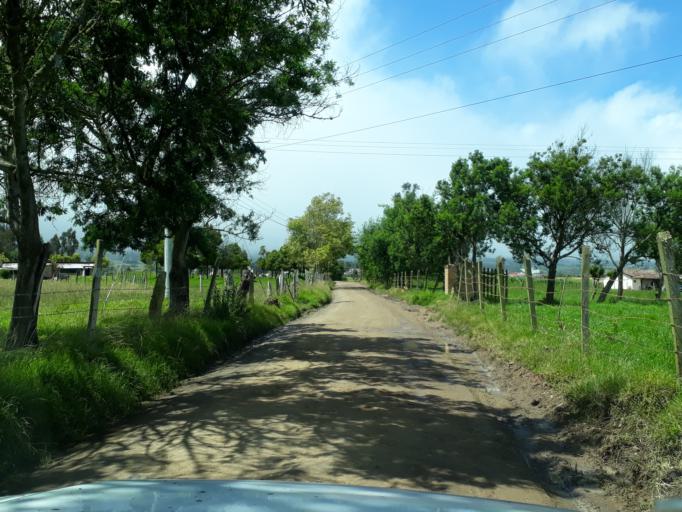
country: CO
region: Cundinamarca
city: Guasca
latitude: 4.8773
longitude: -73.8812
